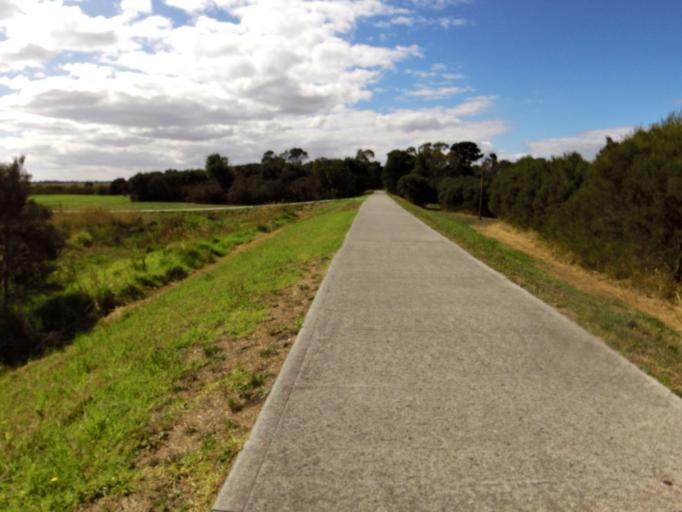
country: AU
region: Victoria
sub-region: Cardinia
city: Koo-Wee-Rup
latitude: -38.2017
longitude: 145.4938
